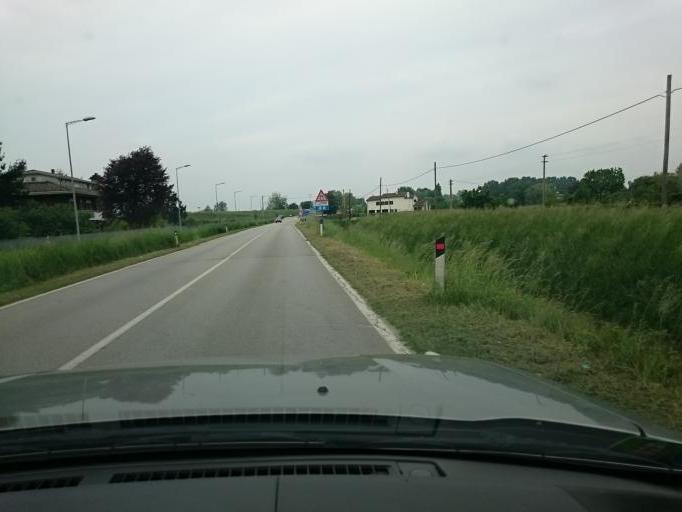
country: IT
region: Veneto
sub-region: Provincia di Padova
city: Bovolenta
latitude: 45.2752
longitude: 11.9321
